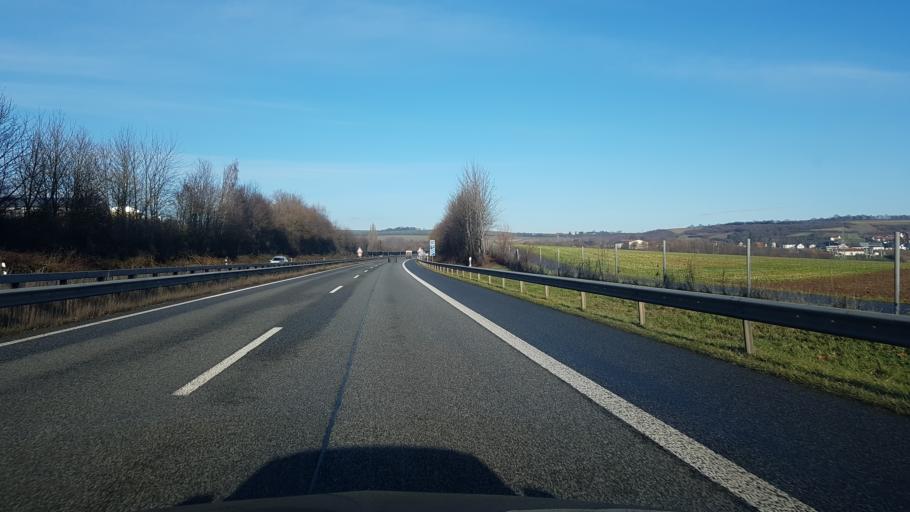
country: DE
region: Rheinland-Pfalz
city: Kirchheimbolanden
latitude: 49.6611
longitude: 8.0252
